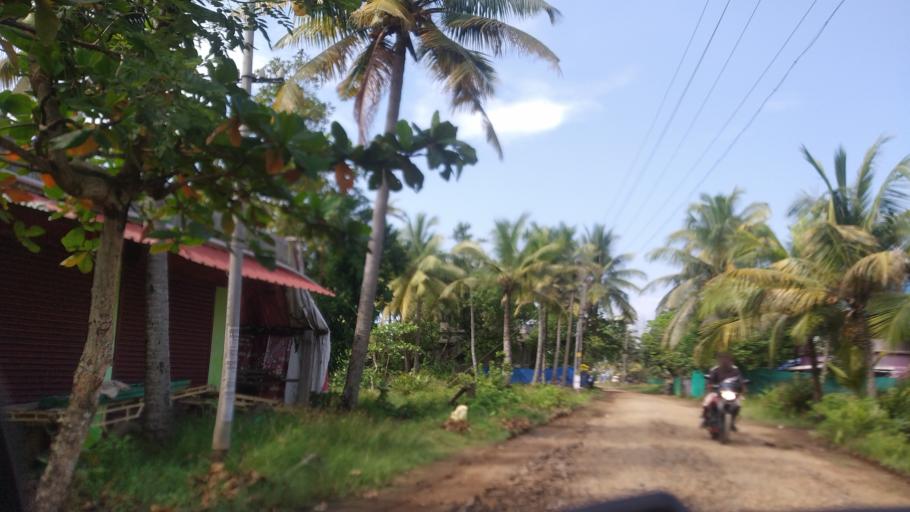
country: IN
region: Kerala
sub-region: Ernakulam
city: Elur
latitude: 10.0576
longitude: 76.2012
